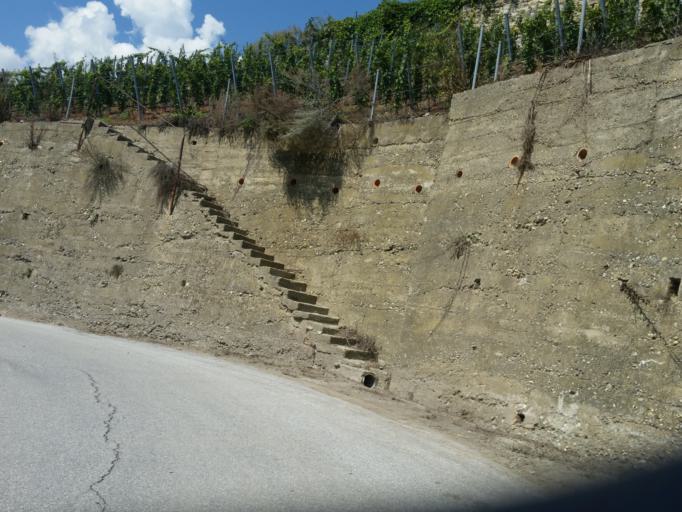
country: CH
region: Valais
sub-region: Sion District
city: Saviese
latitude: 46.2368
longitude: 7.3287
